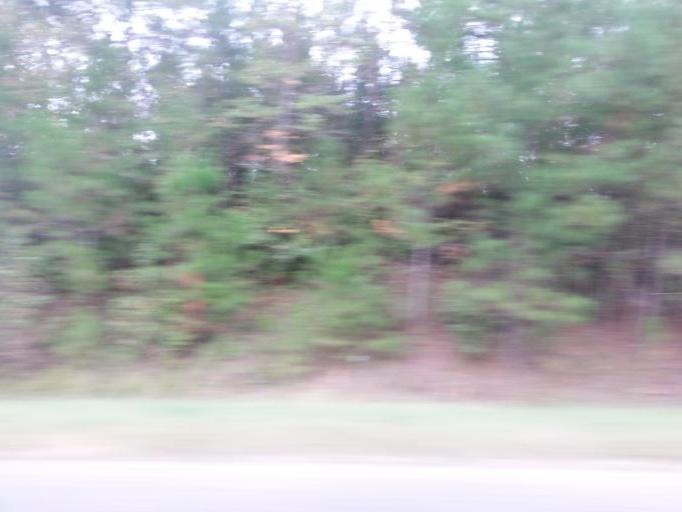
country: US
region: Alabama
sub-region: Butler County
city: Georgiana
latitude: 31.6217
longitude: -86.8047
